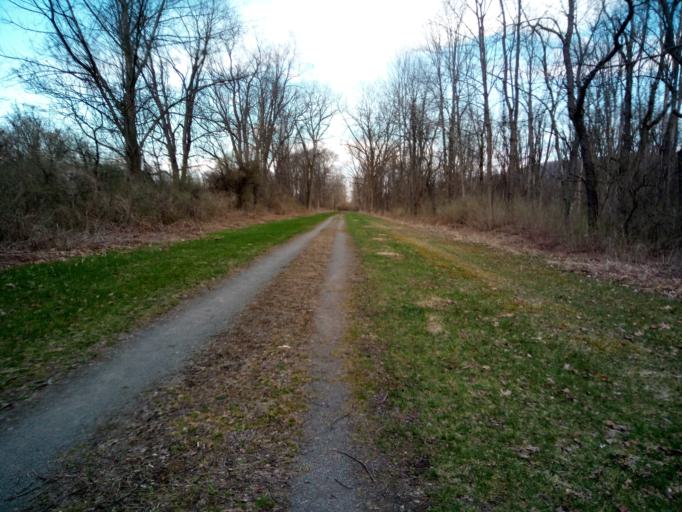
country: US
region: New York
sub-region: Chemung County
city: Big Flats
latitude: 42.1481
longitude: -76.8979
